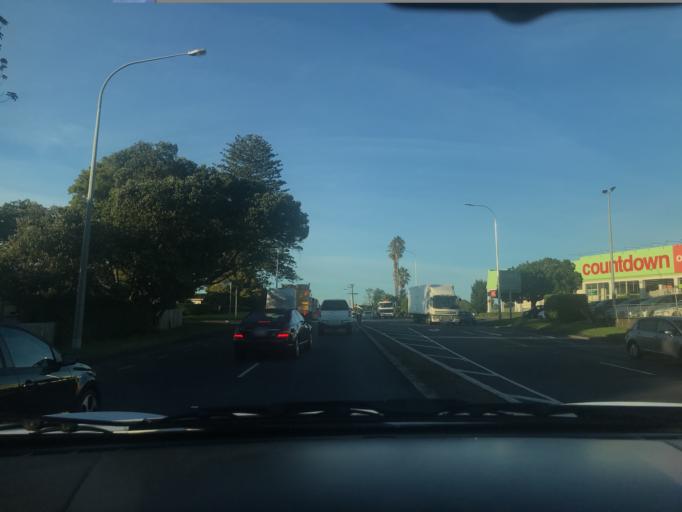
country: NZ
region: Auckland
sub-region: Auckland
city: Tamaki
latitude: -36.9091
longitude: 174.8384
